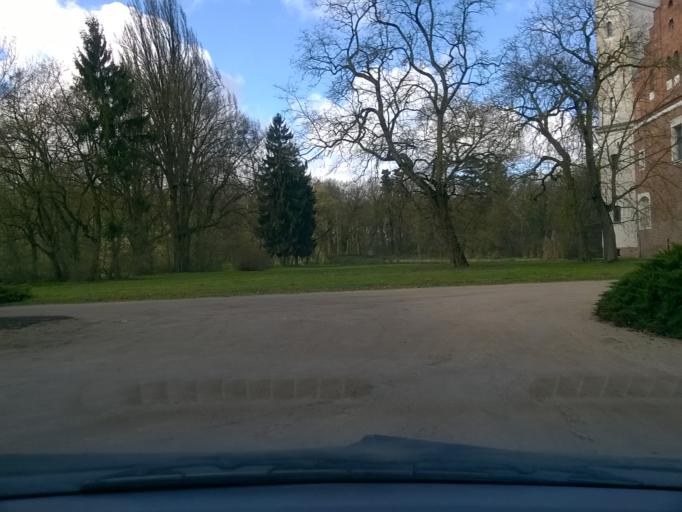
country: PL
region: Kujawsko-Pomorskie
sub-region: Powiat nakielski
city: Kcynia
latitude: 52.9883
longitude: 17.4242
